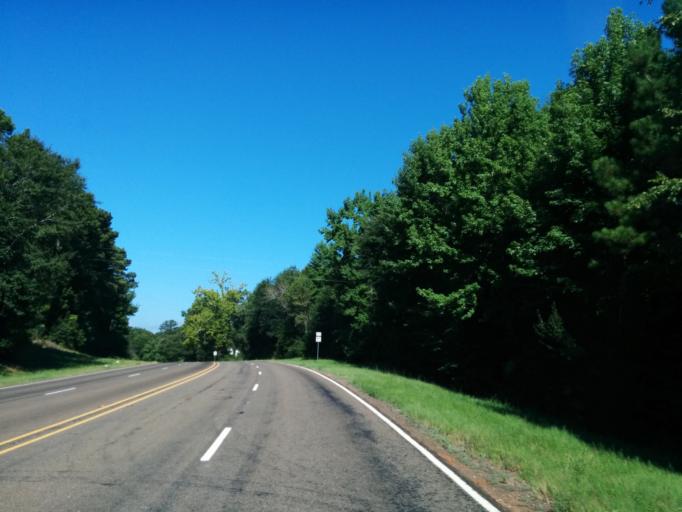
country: US
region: Texas
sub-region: Sabine County
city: Milam
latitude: 31.4338
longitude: -93.8397
